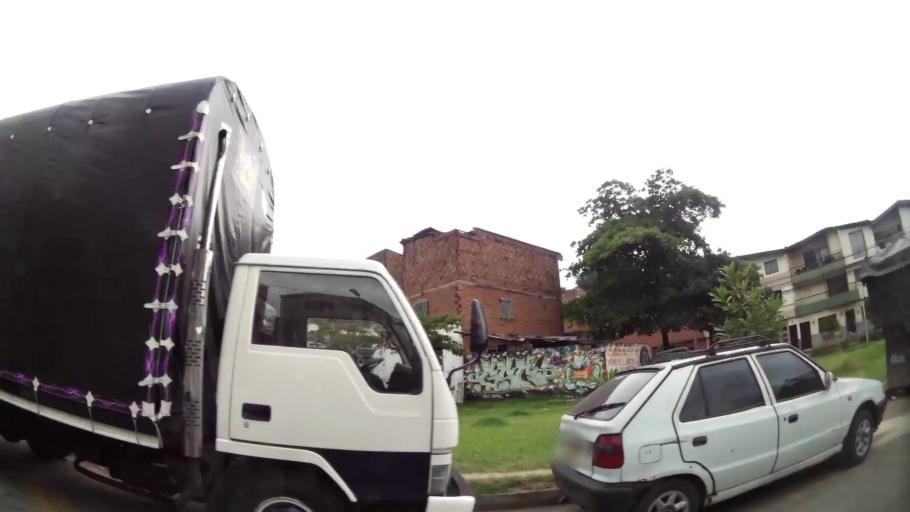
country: CO
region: Antioquia
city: Medellin
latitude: 6.2398
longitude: -75.5600
